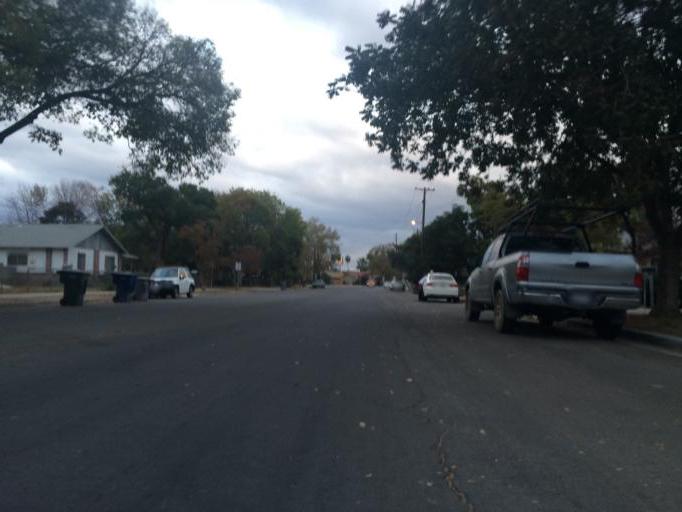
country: US
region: California
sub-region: Fresno County
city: Fresno
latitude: 36.7308
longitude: -119.8065
